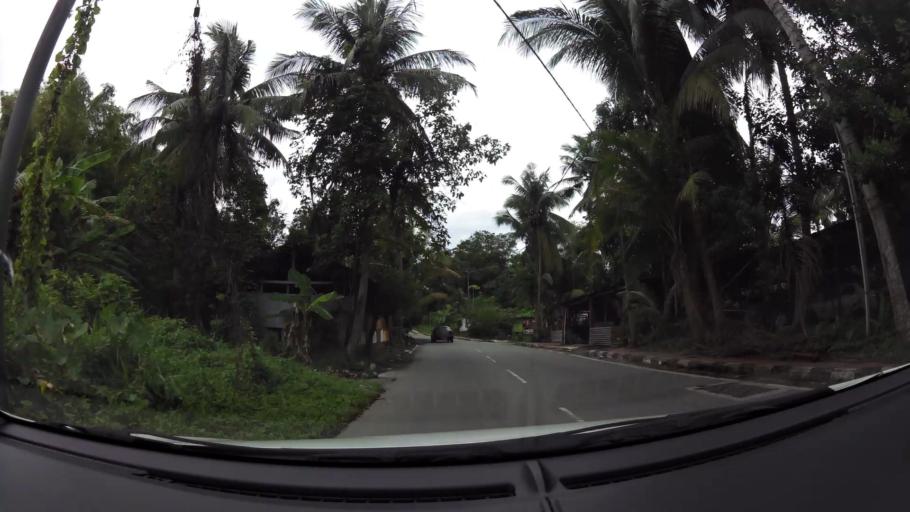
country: BN
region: Brunei and Muara
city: Bandar Seri Begawan
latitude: 4.8951
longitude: 114.9292
